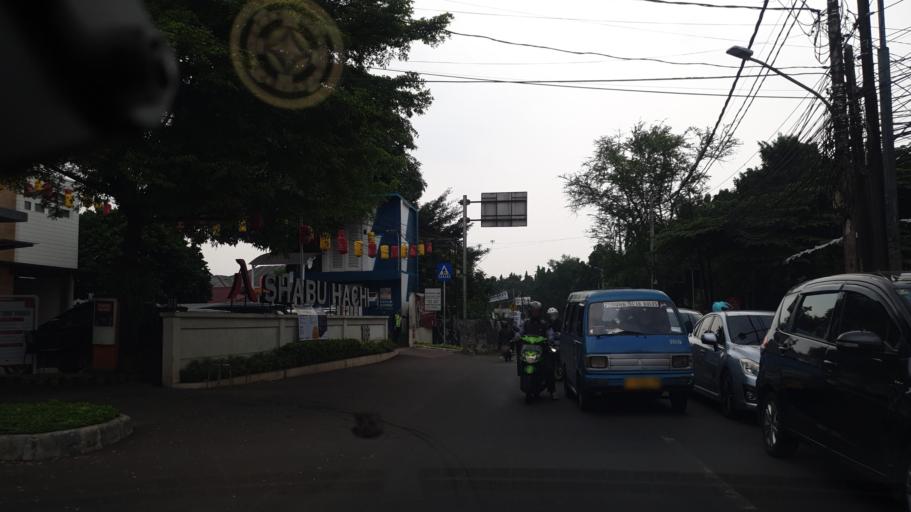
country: ID
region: Banten
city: South Tangerang
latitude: -6.2973
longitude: 106.7737
